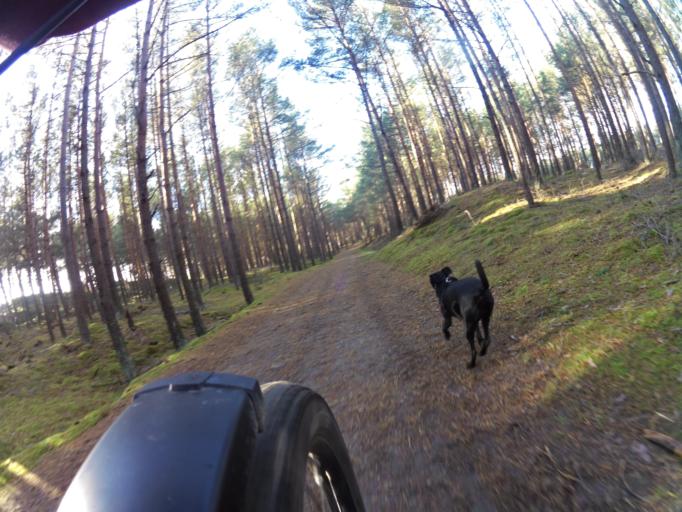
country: PL
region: Pomeranian Voivodeship
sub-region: Powiat wejherowski
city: Choczewo
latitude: 54.8038
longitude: 17.7875
